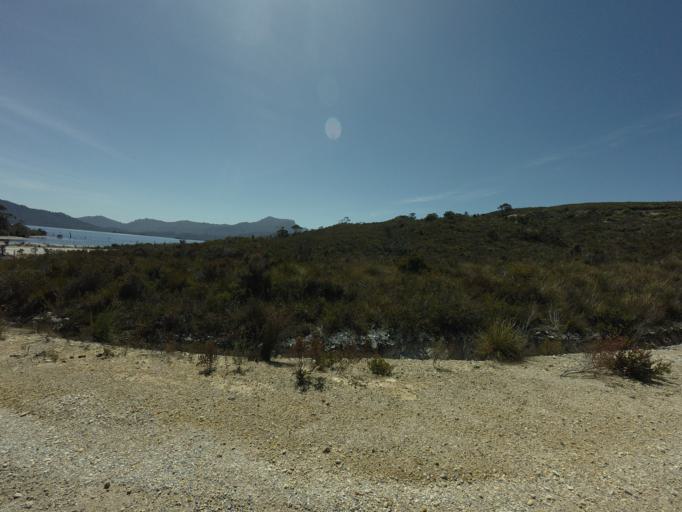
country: AU
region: Tasmania
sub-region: Huon Valley
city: Geeveston
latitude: -43.0325
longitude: 146.3329
